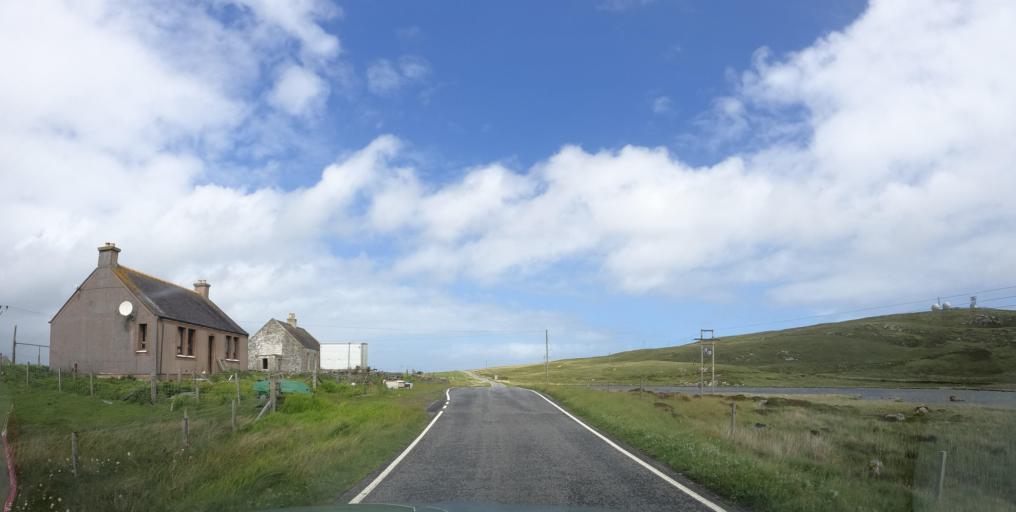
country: GB
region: Scotland
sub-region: Eilean Siar
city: Isle of South Uist
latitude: 57.3377
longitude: -7.3638
